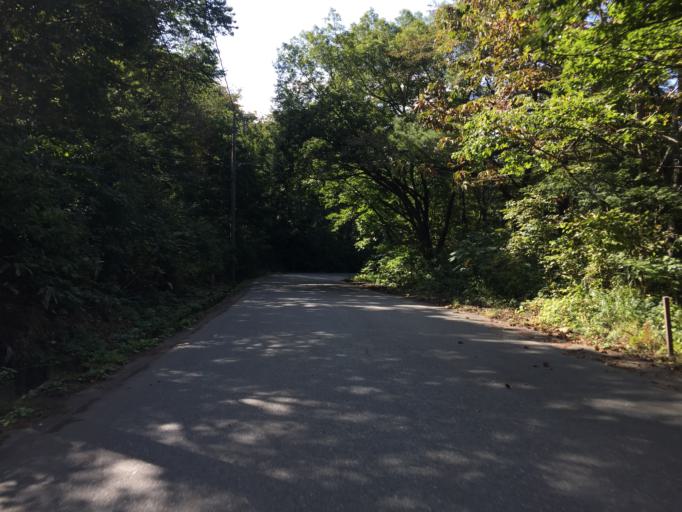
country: JP
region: Yamagata
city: Yonezawa
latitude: 37.8069
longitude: 140.2743
